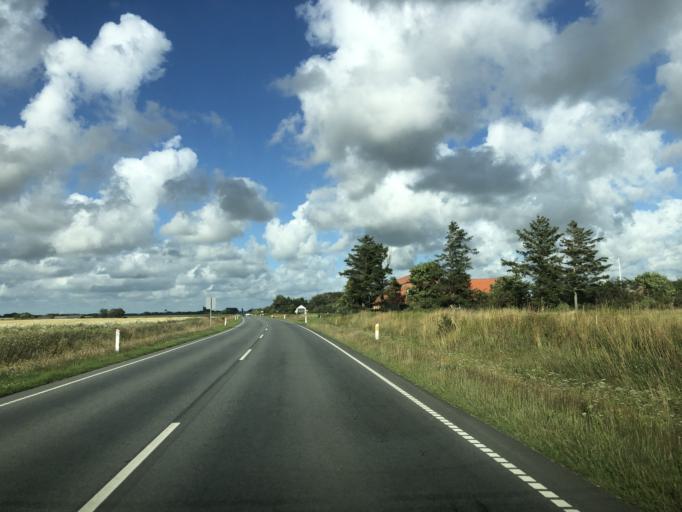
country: DK
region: Central Jutland
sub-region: Lemvig Kommune
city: Lemvig
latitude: 56.5038
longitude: 8.2770
